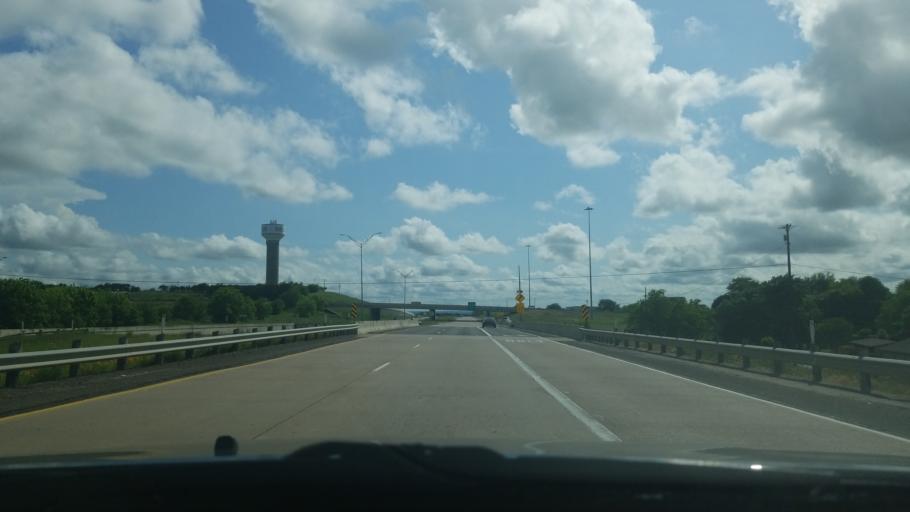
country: US
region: Texas
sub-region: Wise County
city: Decatur
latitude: 33.2419
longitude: -97.5973
